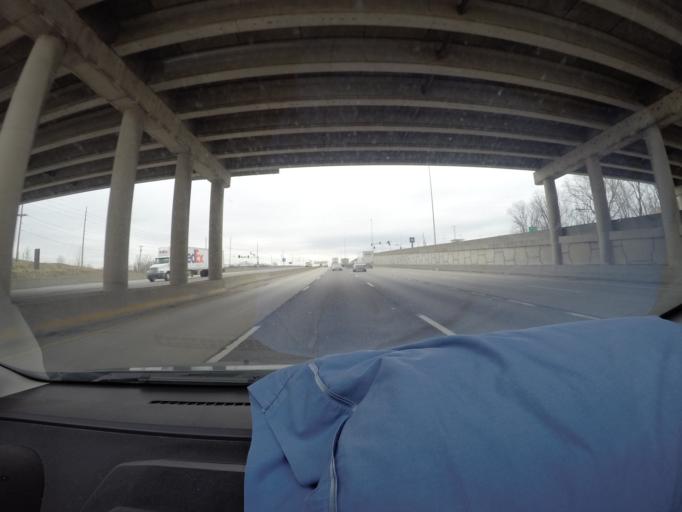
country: US
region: Missouri
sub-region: Saint Charles County
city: Saint Peters
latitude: 38.7984
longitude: -90.6036
